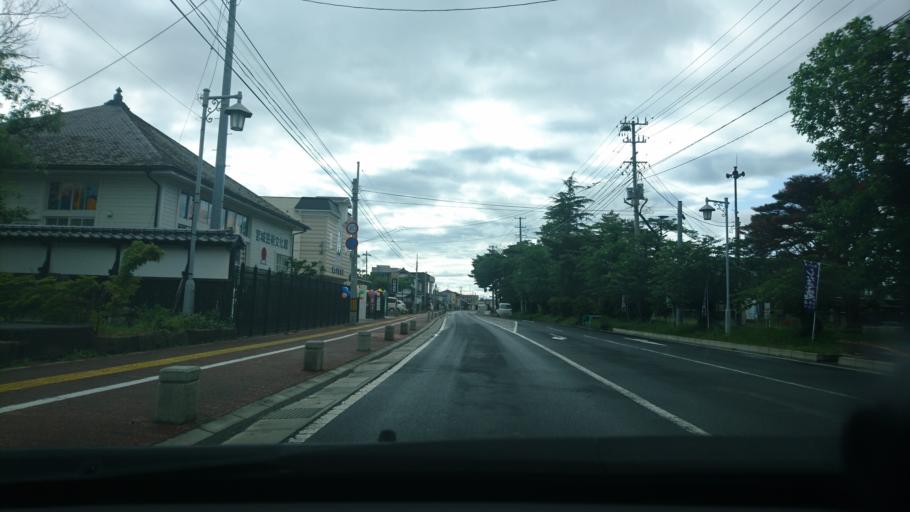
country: JP
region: Miyagi
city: Wakuya
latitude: 38.6545
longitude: 141.2812
